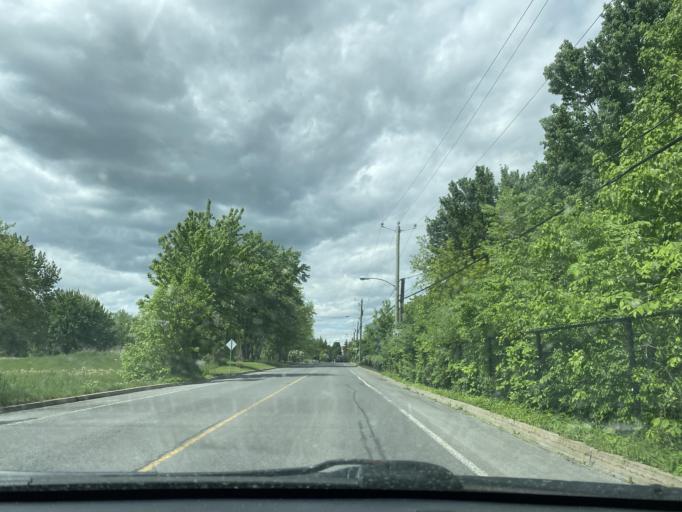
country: CA
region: Quebec
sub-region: Monteregie
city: Carignan
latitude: 45.4639
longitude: -73.2933
